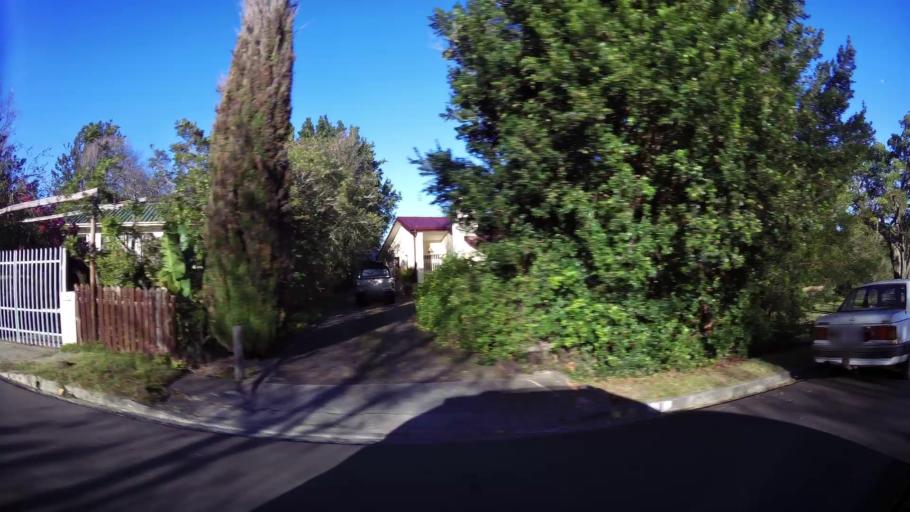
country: ZA
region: Western Cape
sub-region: Eden District Municipality
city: George
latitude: -33.9583
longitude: 22.4494
